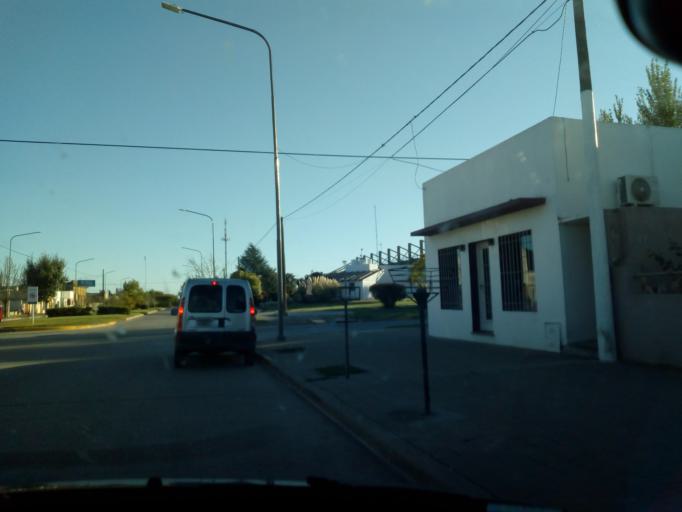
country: AR
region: Buenos Aires
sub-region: Partido de Loberia
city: Loberia
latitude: -38.1581
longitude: -58.7764
